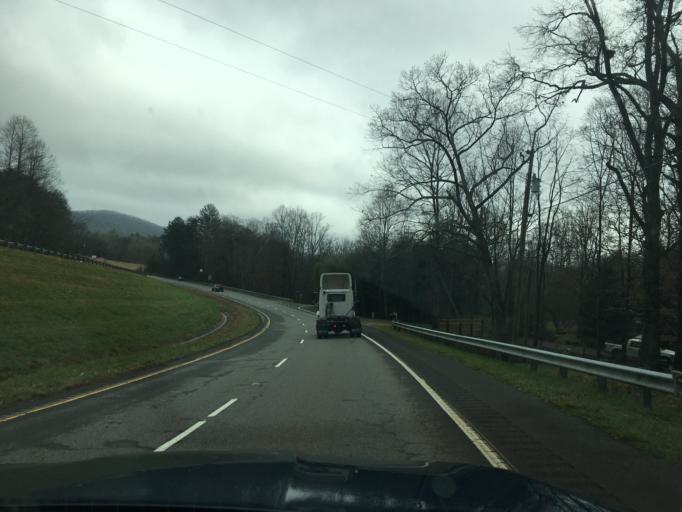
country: US
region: Georgia
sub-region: Fannin County
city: McCaysville
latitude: 35.0156
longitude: -84.3126
